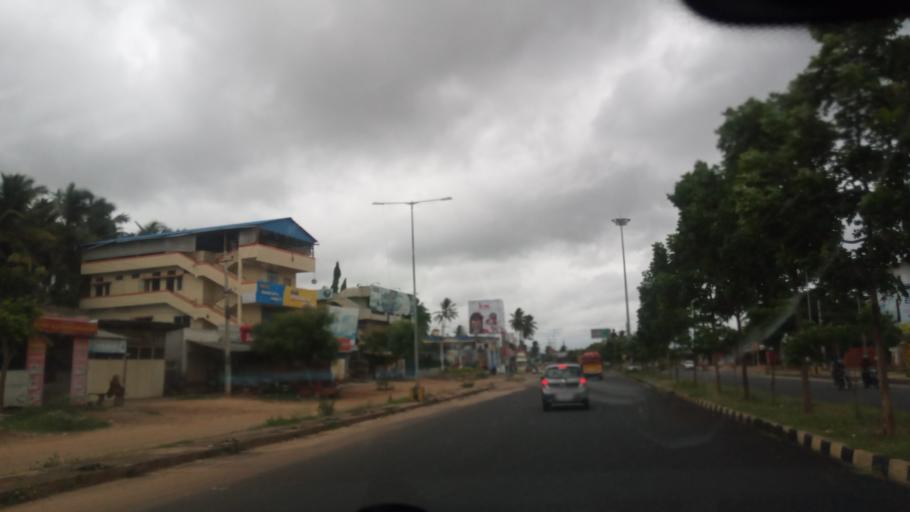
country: IN
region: Karnataka
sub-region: Mysore
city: Mysore
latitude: 12.3037
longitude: 76.6020
